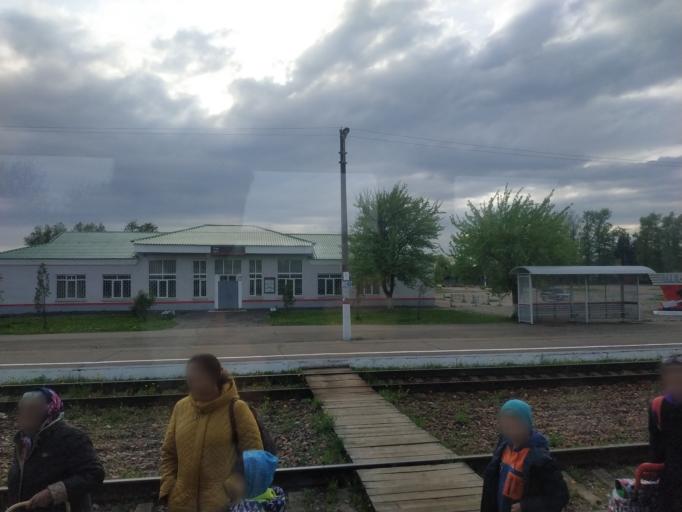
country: RU
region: Smolensk
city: Ugra
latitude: 54.7783
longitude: 34.3424
